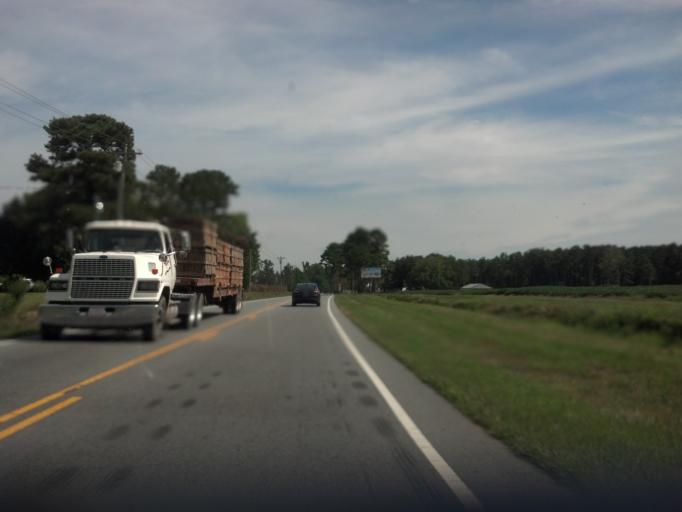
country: US
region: North Carolina
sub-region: Greene County
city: Maury
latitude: 35.5306
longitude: -77.6078
